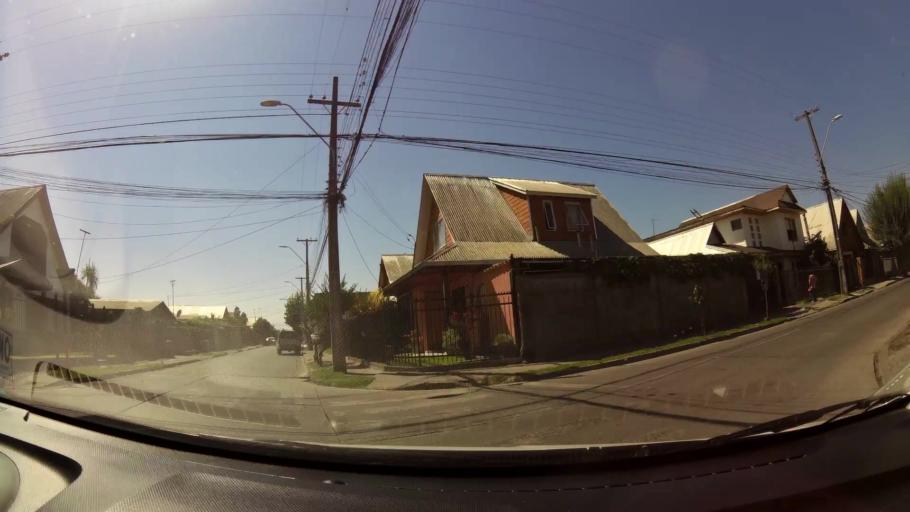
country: CL
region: Maule
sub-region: Provincia de Curico
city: Curico
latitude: -34.9672
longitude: -71.2438
